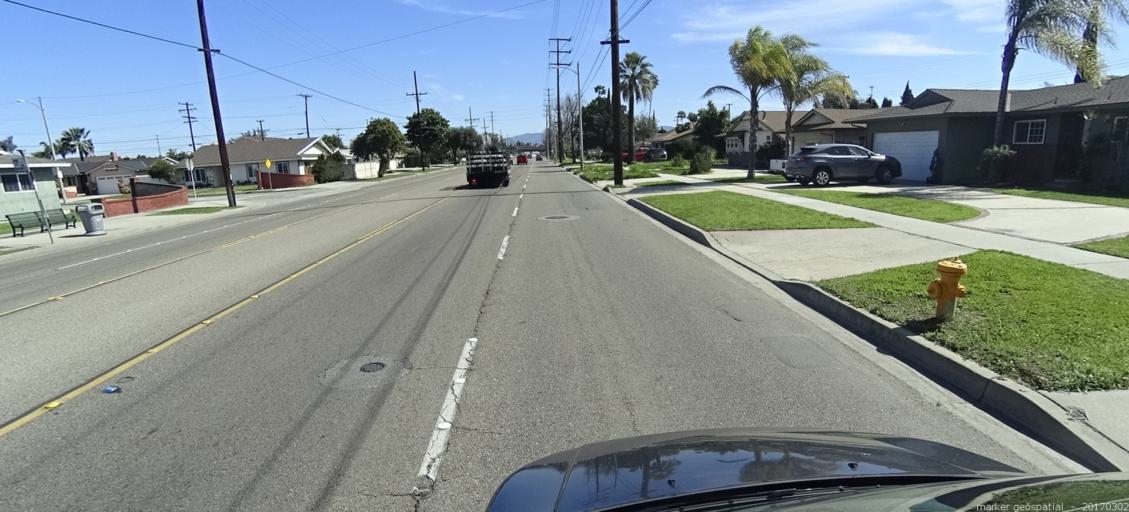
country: US
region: California
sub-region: Orange County
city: Placentia
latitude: 33.8472
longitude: -117.8835
